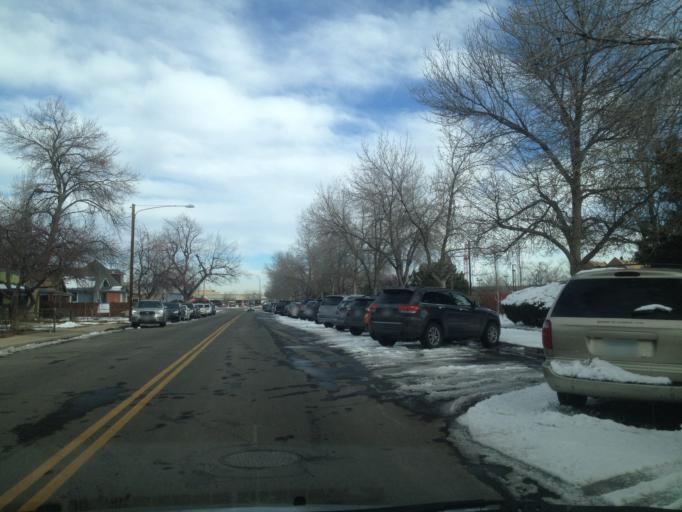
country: US
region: Colorado
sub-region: Boulder County
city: Boulder
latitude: 40.0229
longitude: -105.2610
